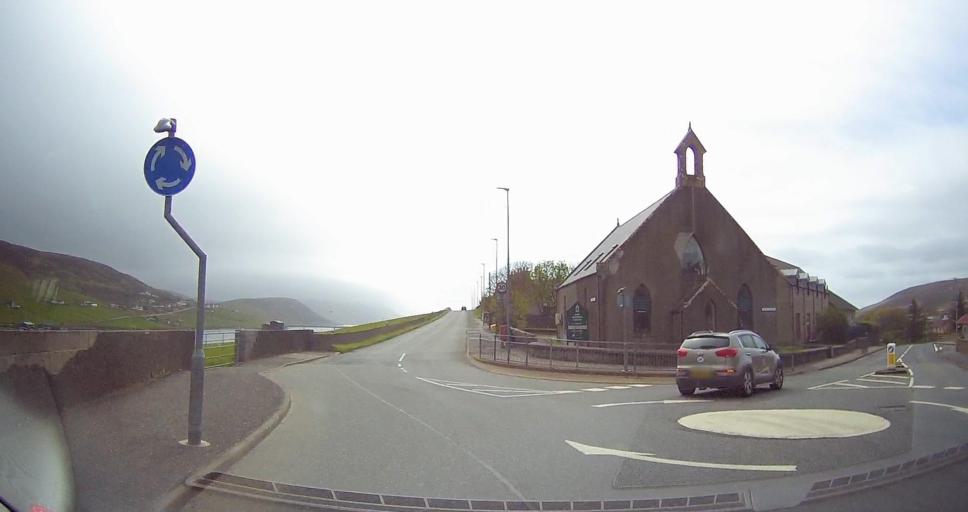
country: GB
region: Scotland
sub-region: Shetland Islands
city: Lerwick
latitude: 60.1402
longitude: -1.2714
